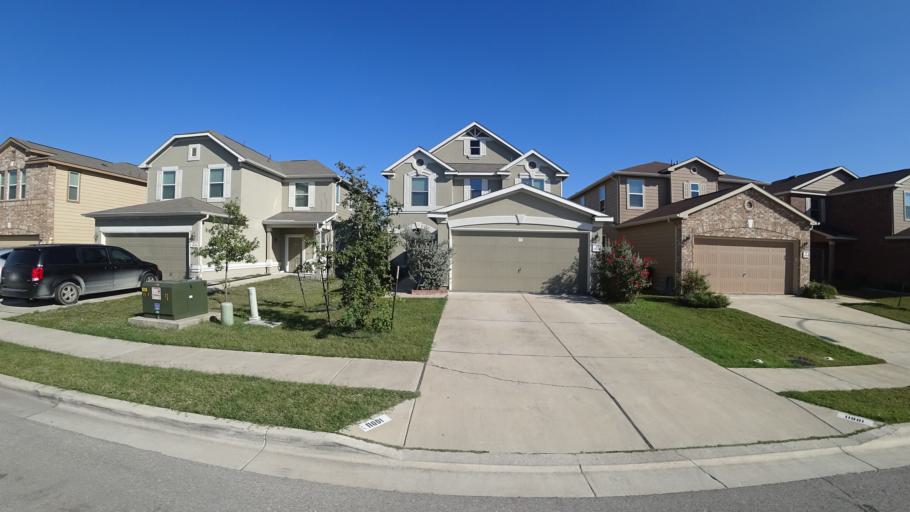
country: US
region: Texas
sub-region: Travis County
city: Manor
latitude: 30.3457
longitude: -97.6150
